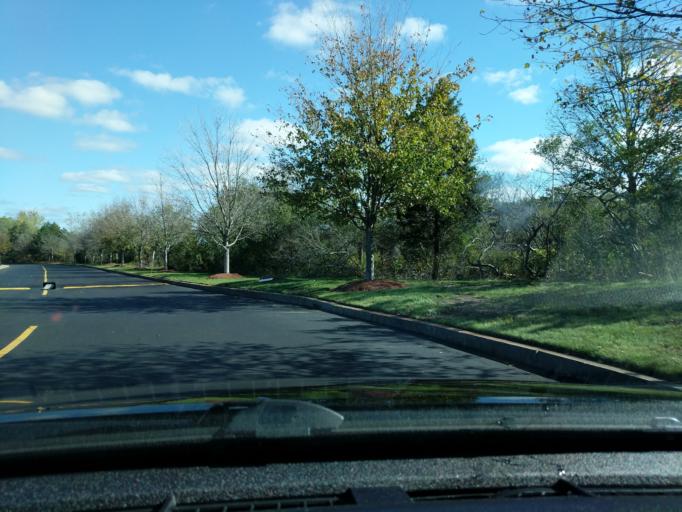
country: US
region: Massachusetts
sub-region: Norfolk County
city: Braintree
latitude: 42.2285
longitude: -71.0173
